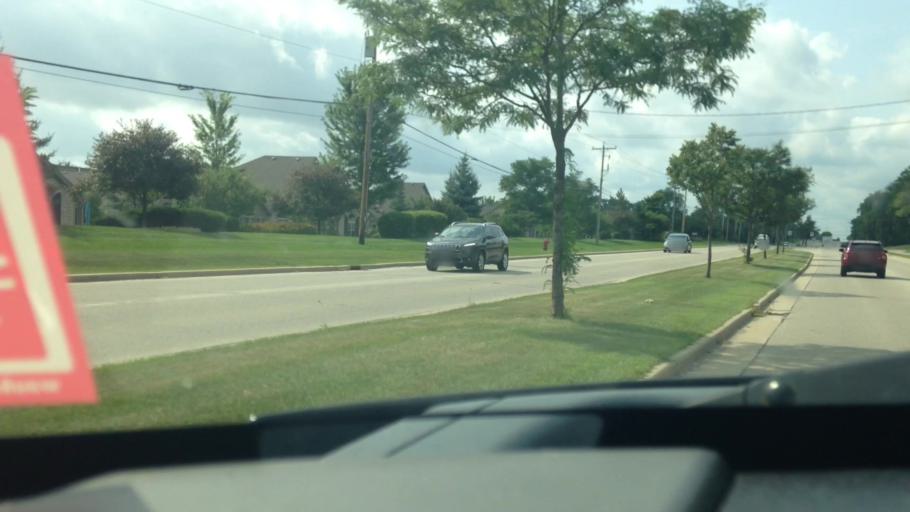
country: US
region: Wisconsin
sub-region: Waukesha County
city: Menomonee Falls
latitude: 43.1460
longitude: -88.1046
